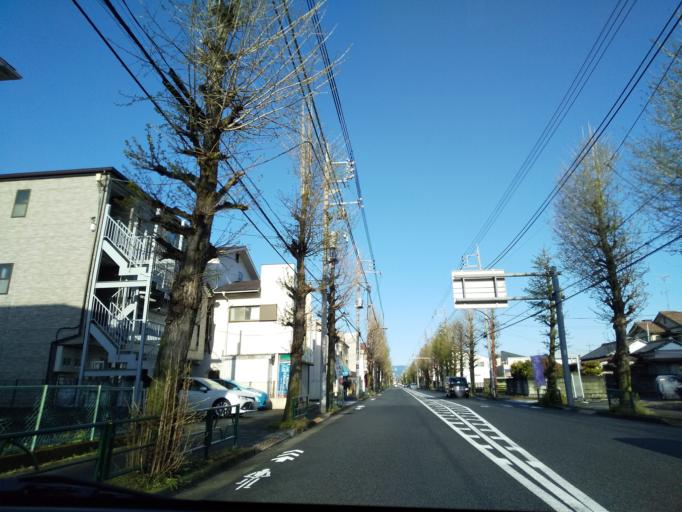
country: JP
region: Tokyo
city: Hino
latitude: 35.6592
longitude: 139.3676
